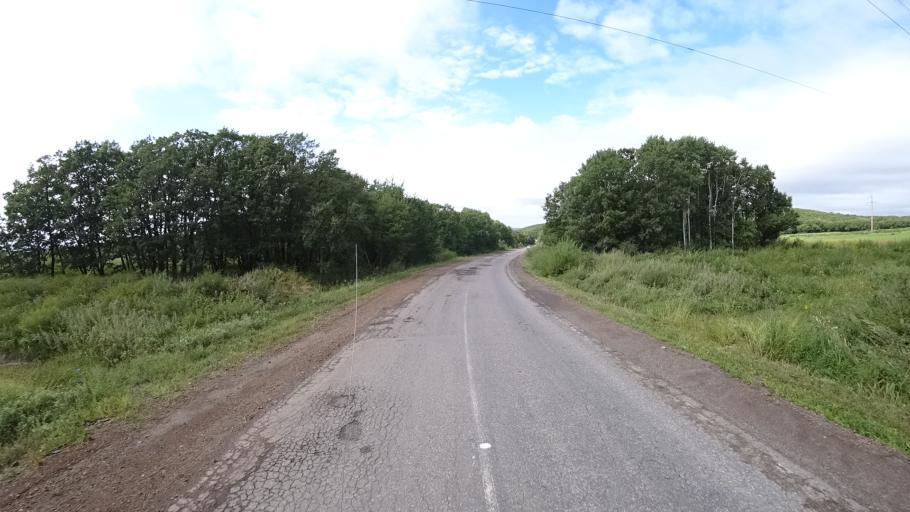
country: RU
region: Primorskiy
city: Lyalichi
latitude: 44.1428
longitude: 132.4039
